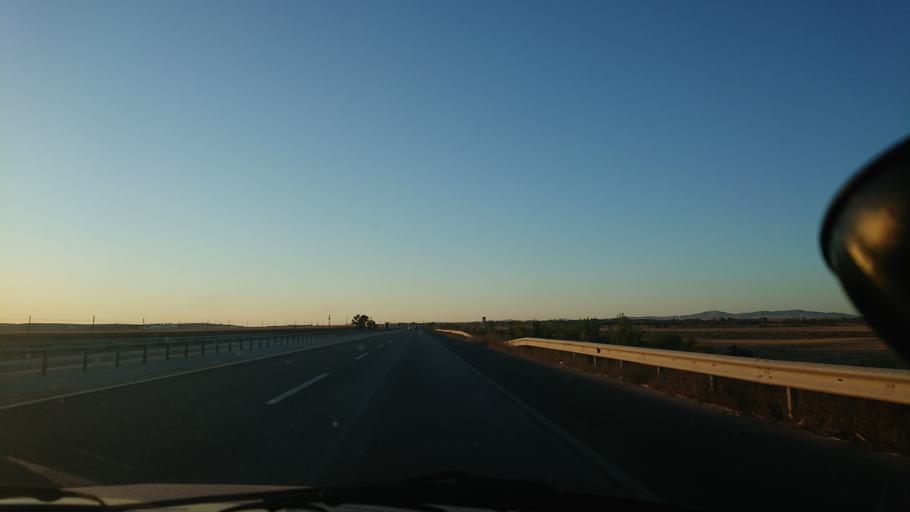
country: TR
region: Eskisehir
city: Mahmudiye
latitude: 39.5466
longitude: 30.9316
